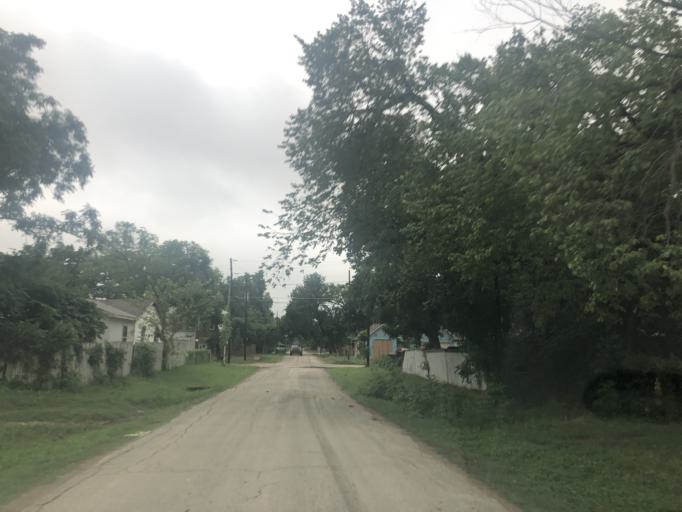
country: US
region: Texas
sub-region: Dallas County
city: Cockrell Hill
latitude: 32.7860
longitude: -96.8808
